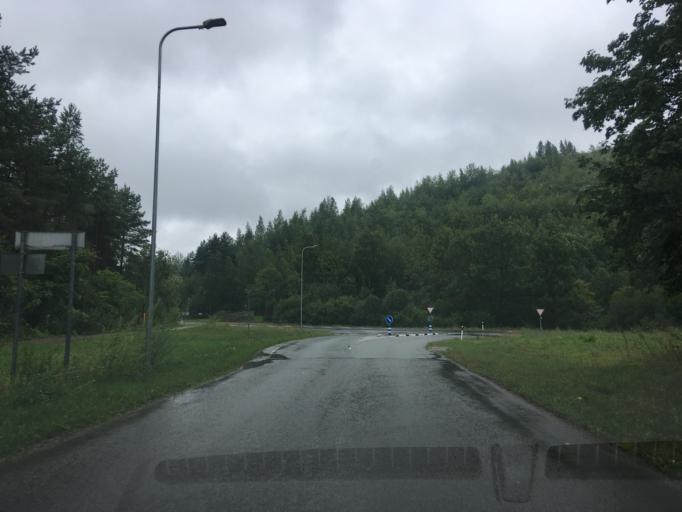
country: EE
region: Ida-Virumaa
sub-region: Kivioli linn
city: Kivioli
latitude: 59.3591
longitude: 26.9560
